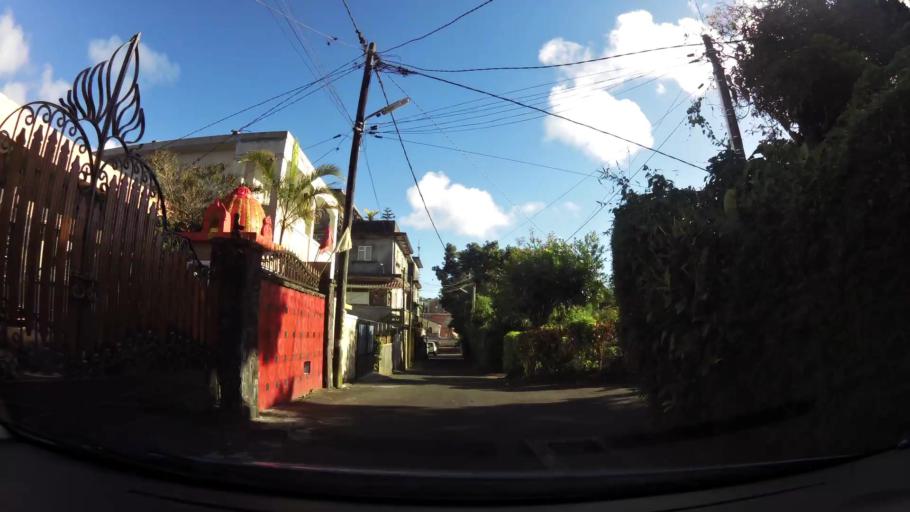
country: MU
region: Plaines Wilhems
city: Curepipe
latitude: -20.3173
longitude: 57.5374
